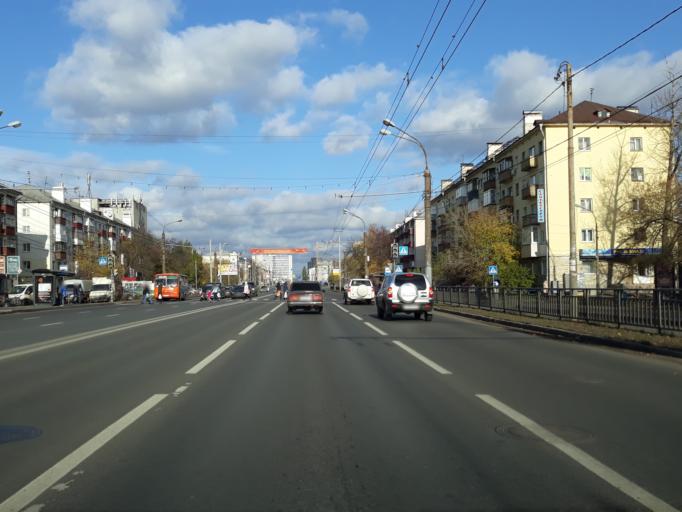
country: RU
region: Nizjnij Novgorod
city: Nizhniy Novgorod
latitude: 56.2934
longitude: 43.9342
